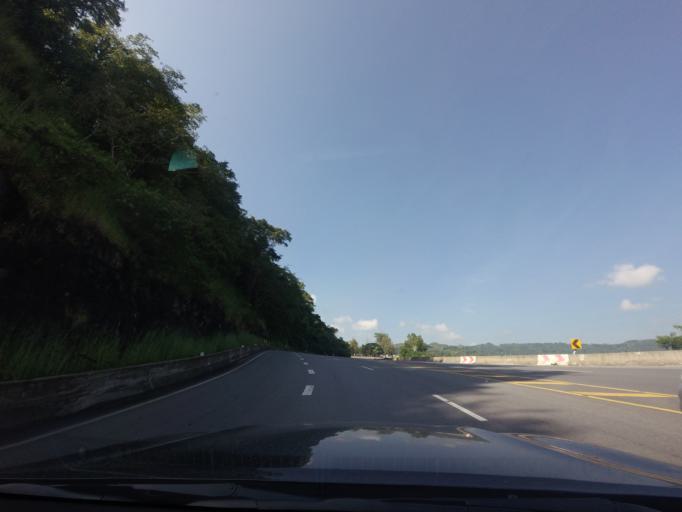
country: TH
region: Phetchabun
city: Khao Kho
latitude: 16.7843
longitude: 101.0862
